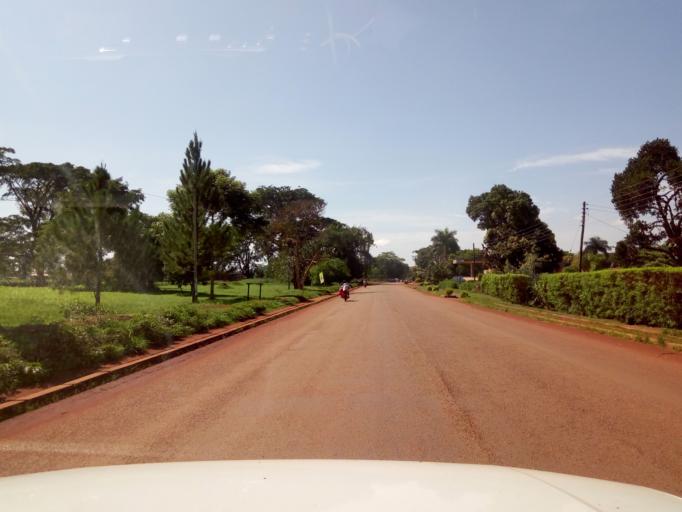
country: UG
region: Western Region
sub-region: Masindi District
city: Masindi
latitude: 1.6885
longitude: 31.7159
